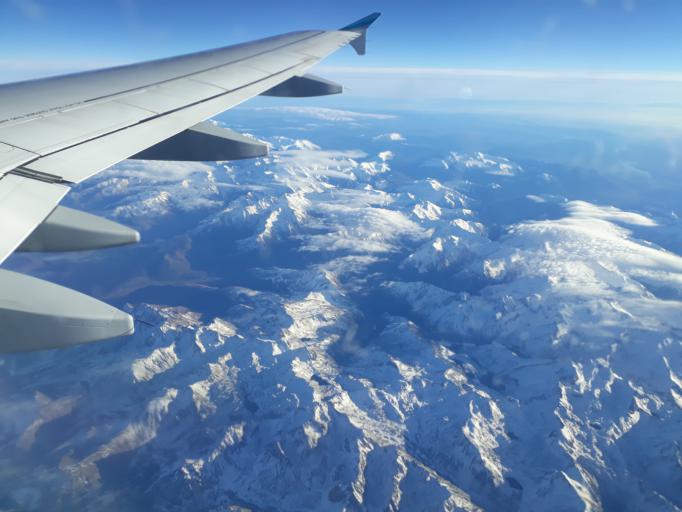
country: FR
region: Midi-Pyrenees
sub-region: Departement des Hautes-Pyrenees
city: Campan
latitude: 42.9727
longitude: 0.0885
